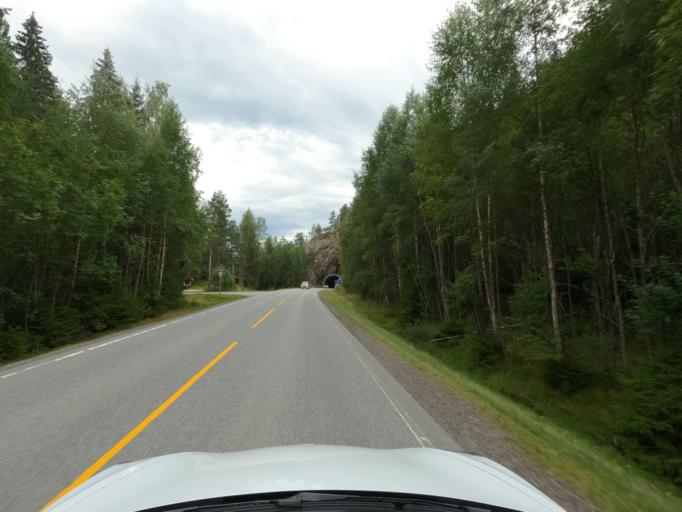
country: NO
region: Telemark
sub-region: Hjartdal
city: Sauland
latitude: 59.7376
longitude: 9.0200
